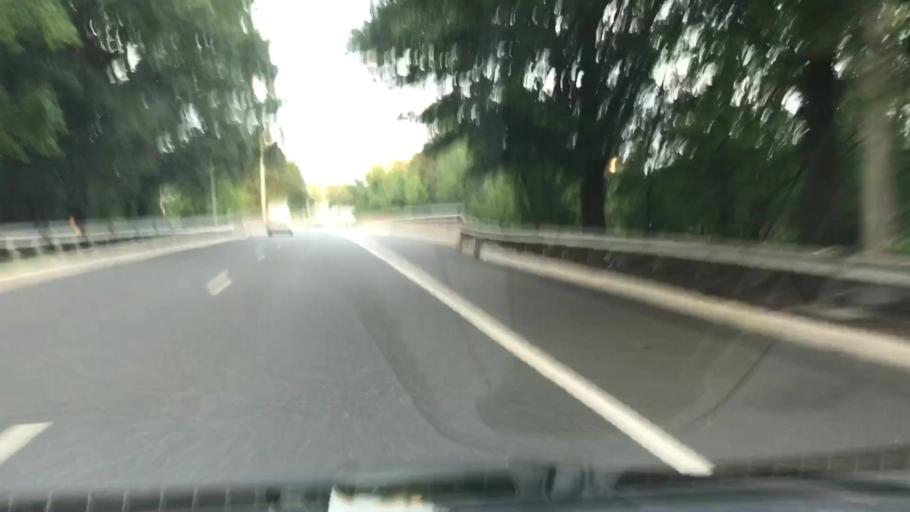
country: US
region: New Jersey
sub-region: Camden County
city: Pennsauken
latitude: 39.9744
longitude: -75.0311
